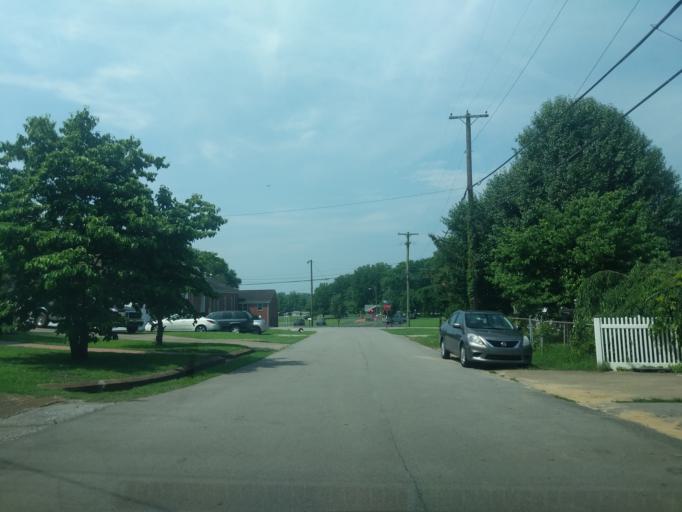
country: US
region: Tennessee
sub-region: Davidson County
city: Lakewood
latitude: 36.2715
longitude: -86.6670
